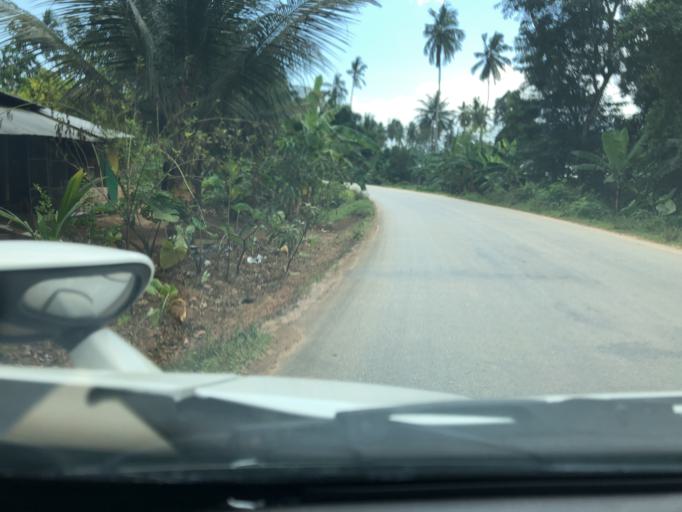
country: TZ
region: Zanzibar Central/South
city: Koani
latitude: -6.0813
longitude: 39.2534
